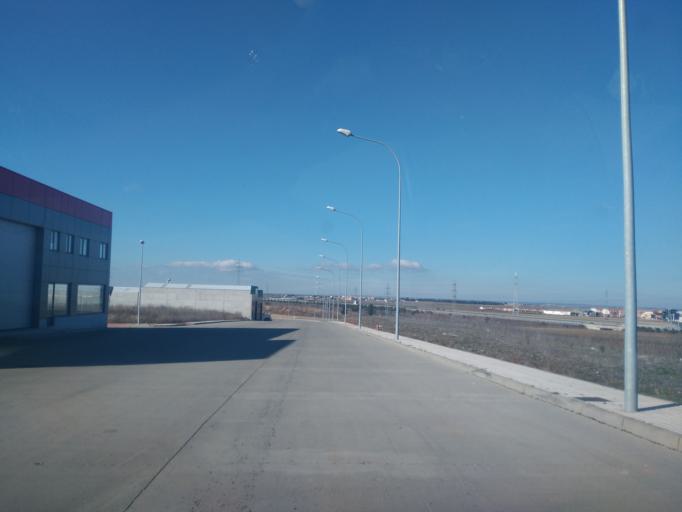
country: ES
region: Castille and Leon
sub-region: Provincia de Salamanca
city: Villares de la Reina
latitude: 40.9972
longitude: -5.6476
